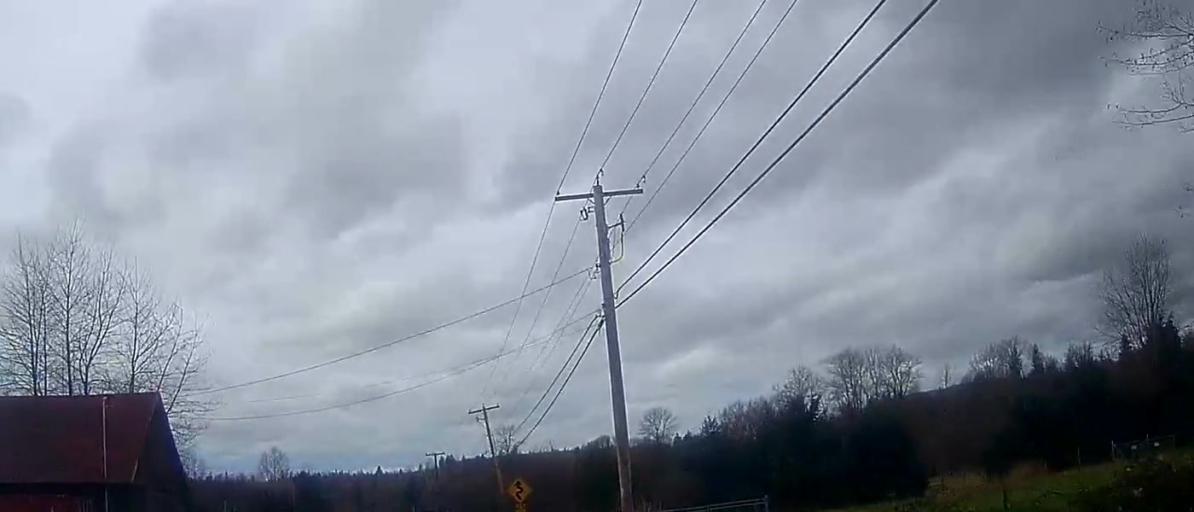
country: US
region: Washington
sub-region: Skagit County
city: Sedro-Woolley
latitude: 48.5835
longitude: -122.2758
